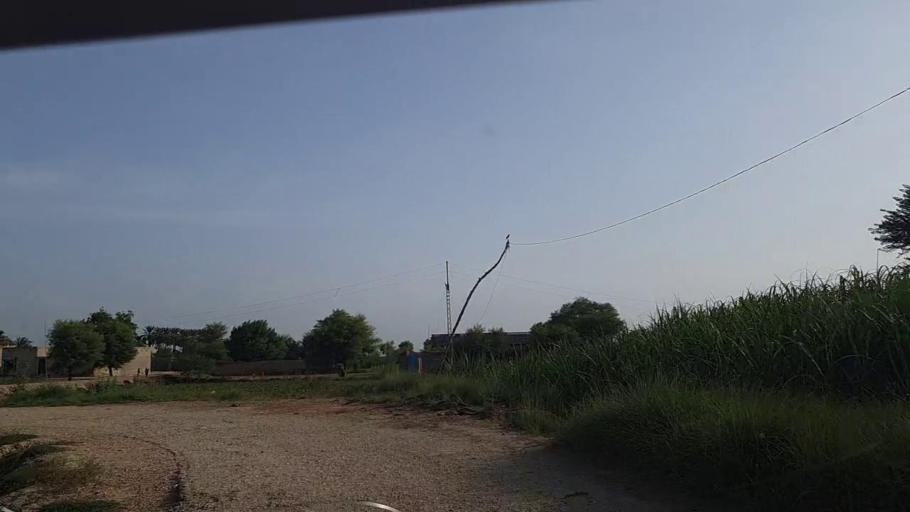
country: PK
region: Sindh
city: Ghotki
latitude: 27.9827
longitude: 69.2528
